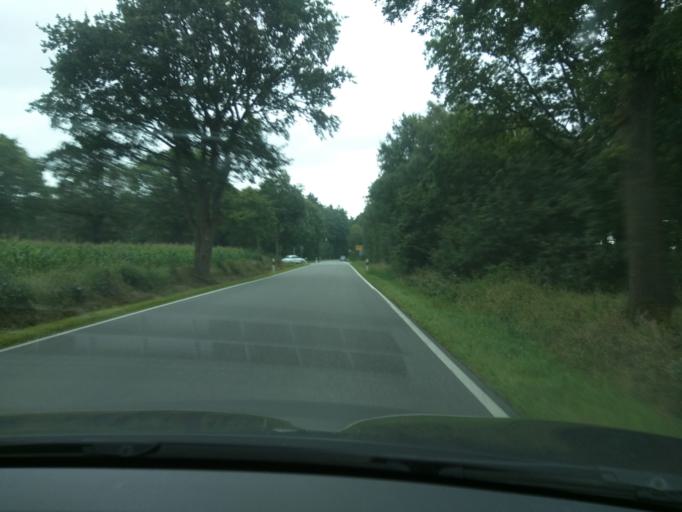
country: DE
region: Schleswig-Holstein
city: Besenthal
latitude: 53.5338
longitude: 10.7237
